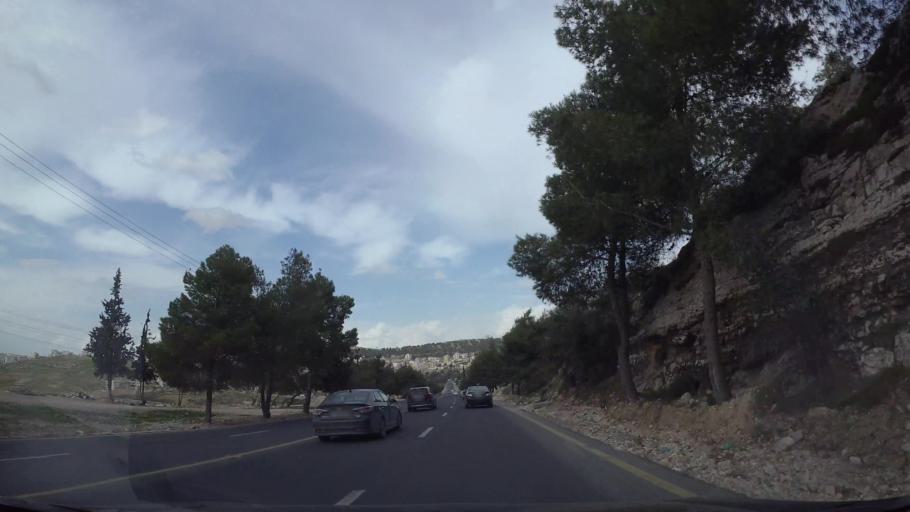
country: JO
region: Amman
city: Amman
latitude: 32.0149
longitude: 35.9350
